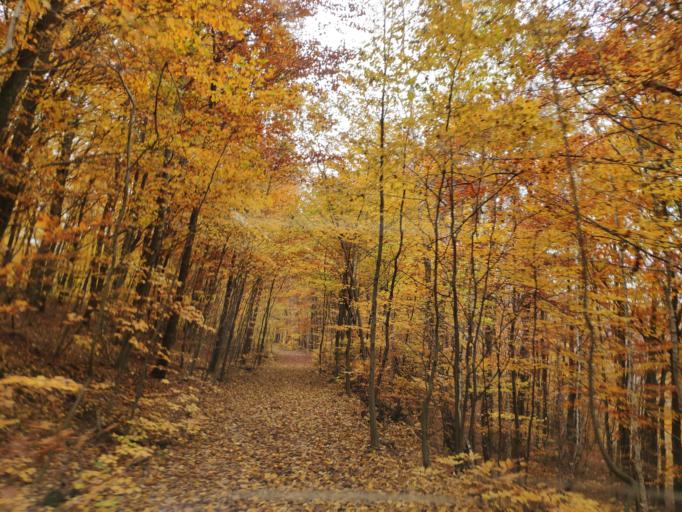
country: SK
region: Kosicky
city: Moldava nad Bodvou
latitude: 48.7270
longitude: 21.0929
